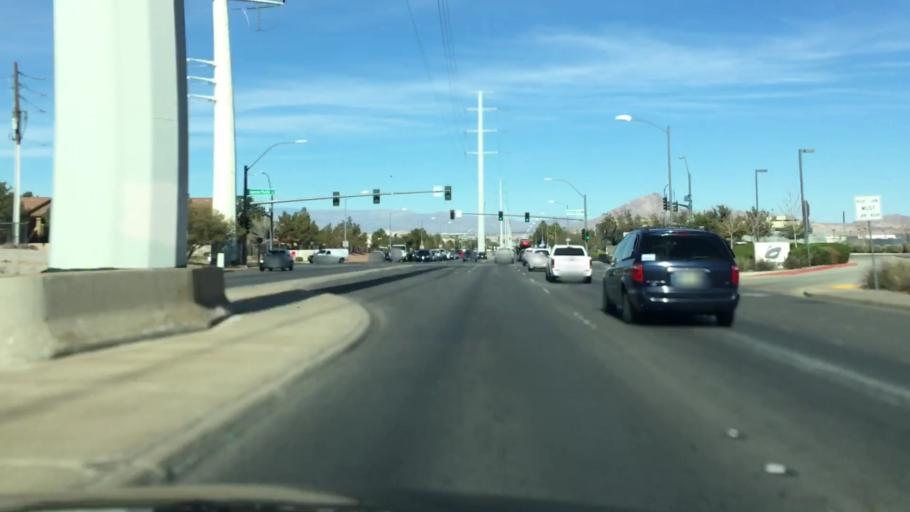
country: US
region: Nevada
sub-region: Clark County
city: Henderson
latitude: 36.0411
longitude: -115.0293
